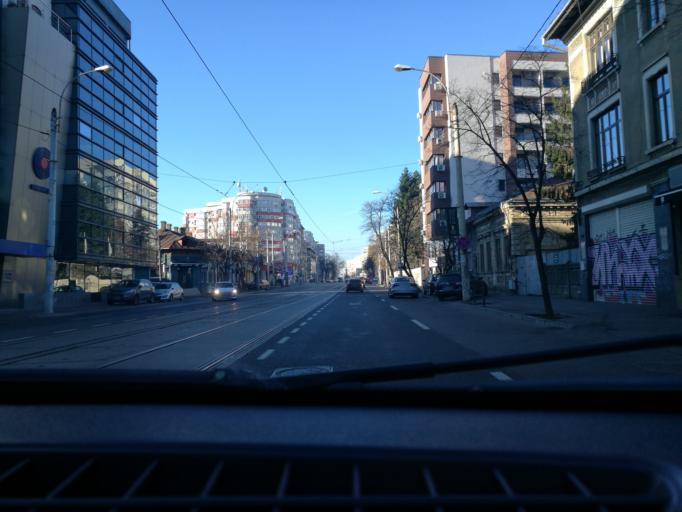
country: RO
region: Bucuresti
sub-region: Municipiul Bucuresti
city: Bucuresti
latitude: 44.4549
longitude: 26.0815
